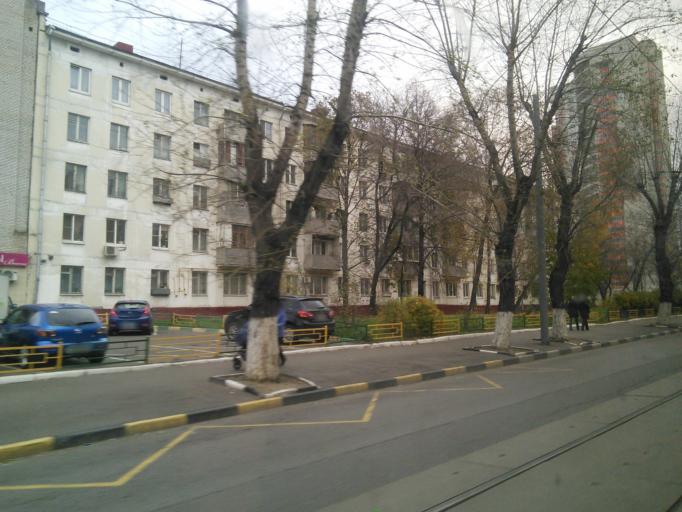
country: RU
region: Moscow
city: Lefortovo
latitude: 55.7612
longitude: 37.7127
